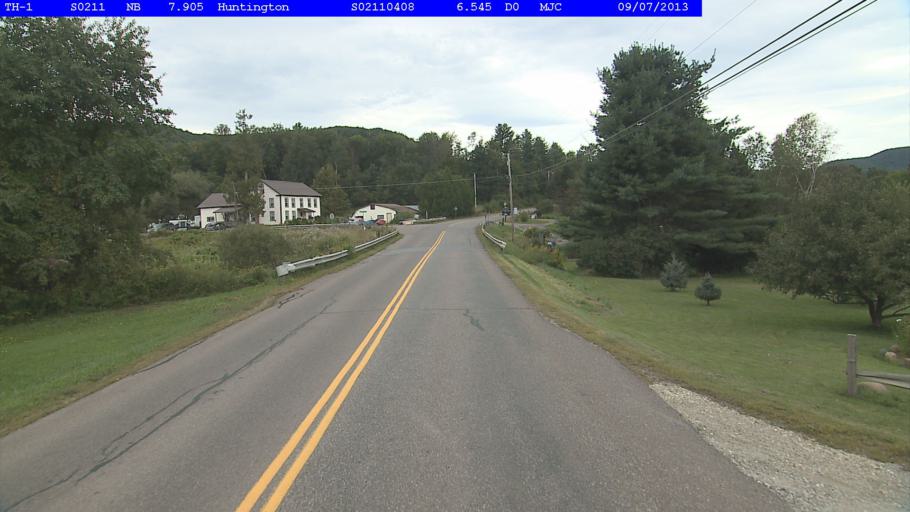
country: US
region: Vermont
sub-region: Chittenden County
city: Hinesburg
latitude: 44.3132
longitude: -72.9883
